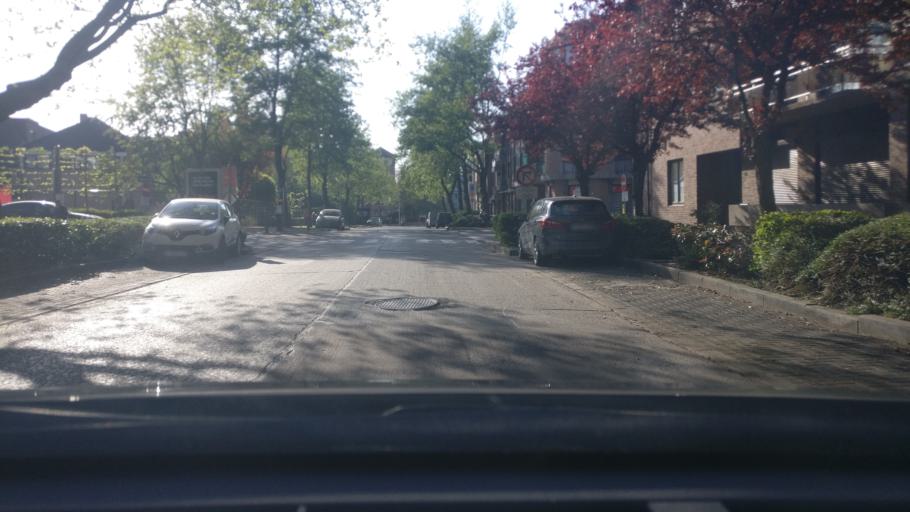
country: BE
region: Flanders
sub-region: Provincie Vlaams-Brabant
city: Kraainem
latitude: 50.8400
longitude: 4.4628
